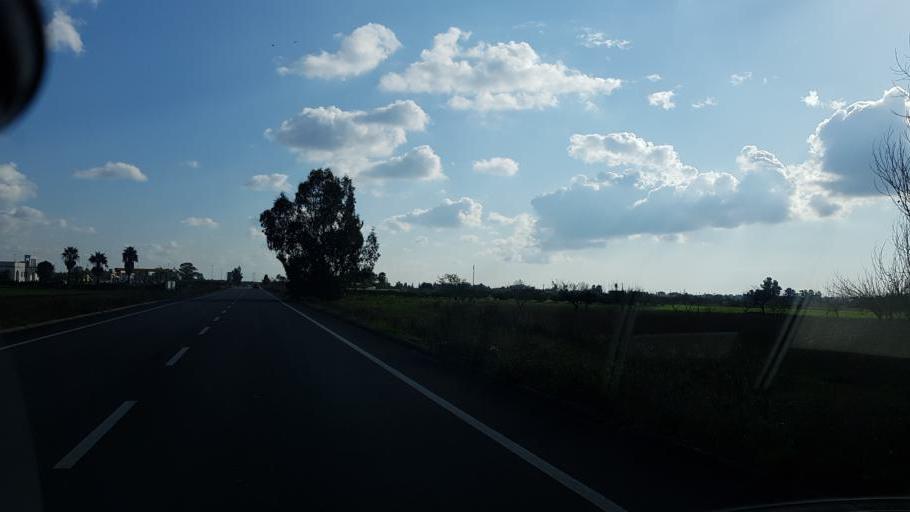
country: IT
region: Apulia
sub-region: Provincia di Lecce
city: Veglie
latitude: 40.3436
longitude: 17.9769
